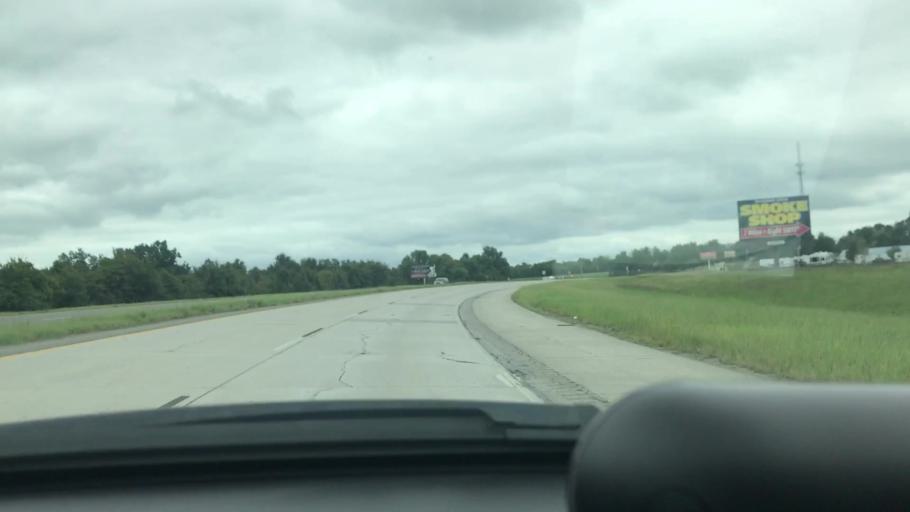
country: US
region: Oklahoma
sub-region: Wagoner County
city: Wagoner
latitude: 35.9128
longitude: -95.4011
